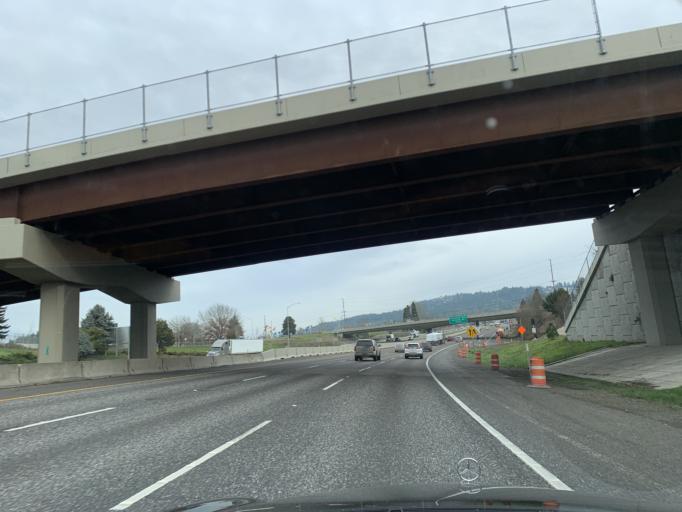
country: US
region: Oregon
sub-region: Clackamas County
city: Clackamas
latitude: 45.4183
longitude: -122.5738
